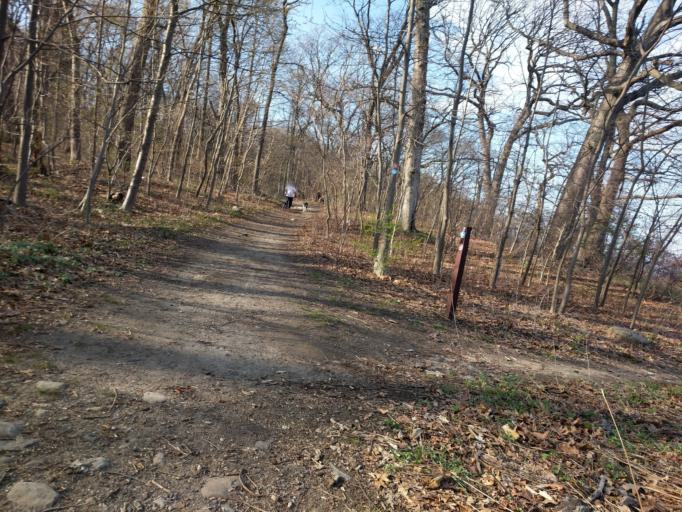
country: US
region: New York
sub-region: Westchester County
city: Pelham Manor
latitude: 40.8726
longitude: -73.7877
